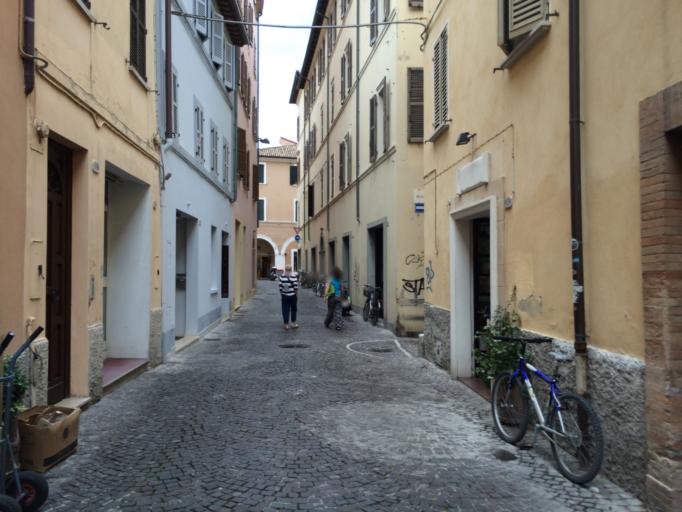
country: IT
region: The Marches
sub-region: Provincia di Pesaro e Urbino
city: Pesaro
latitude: 43.9115
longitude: 12.9119
